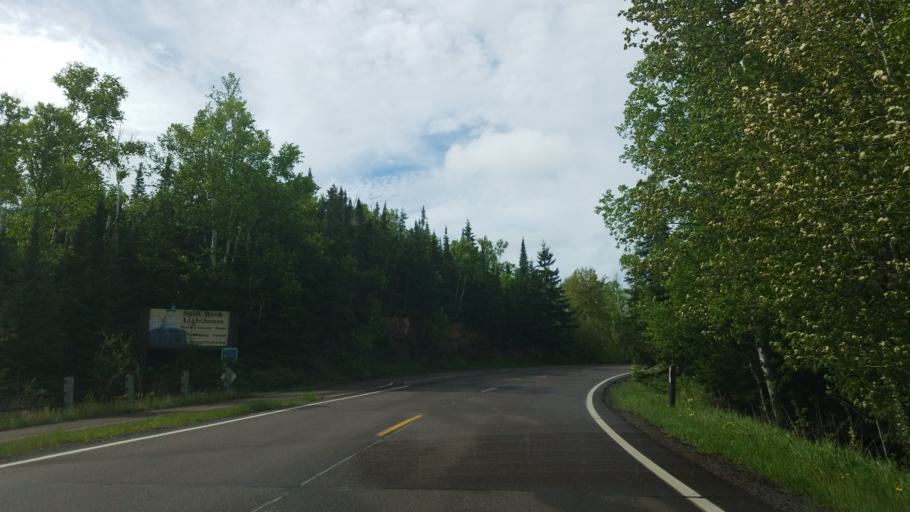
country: US
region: Minnesota
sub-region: Lake County
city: Silver Bay
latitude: 47.2050
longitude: -91.3680
